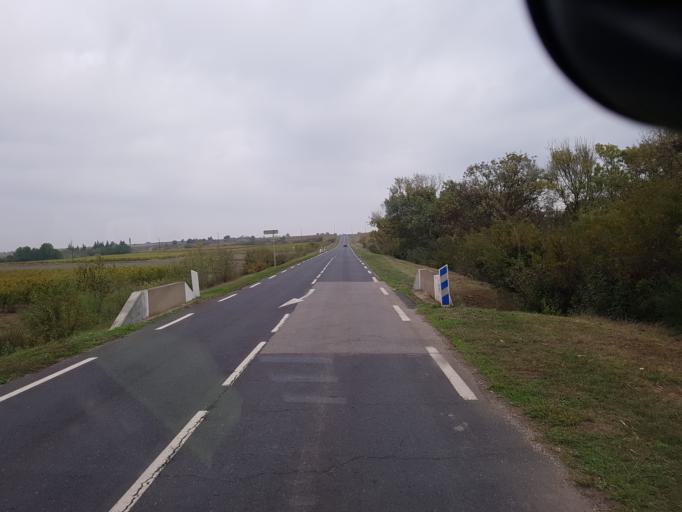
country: FR
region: Languedoc-Roussillon
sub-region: Departement de l'Herault
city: Marseillan
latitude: 43.3672
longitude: 3.5312
